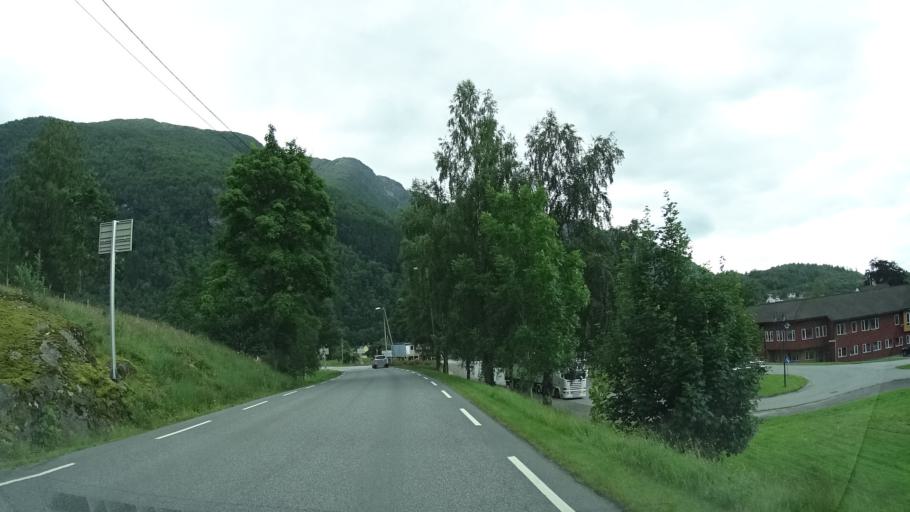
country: NO
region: Hordaland
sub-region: Jondal
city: Jondal
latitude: 60.2800
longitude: 6.2507
